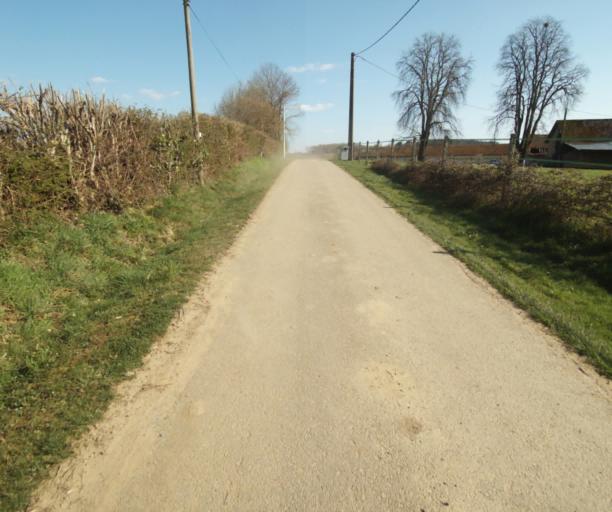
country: FR
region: Limousin
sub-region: Departement de la Correze
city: Saint-Mexant
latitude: 45.3264
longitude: 1.6128
